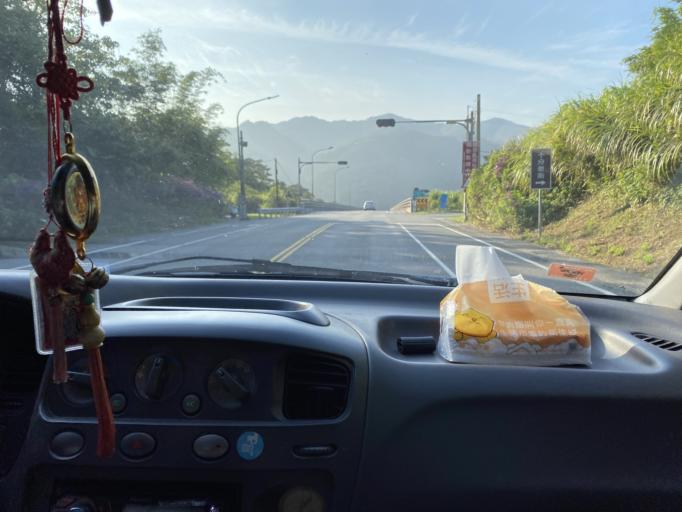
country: TW
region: Taiwan
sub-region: Keelung
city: Keelung
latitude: 25.0489
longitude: 121.7768
